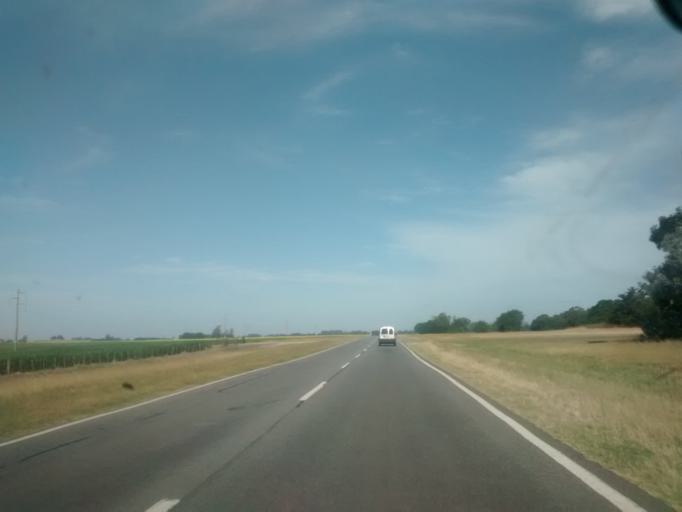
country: AR
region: Buenos Aires
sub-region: Partido de Balcarce
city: Balcarce
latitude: -37.6707
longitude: -58.4991
